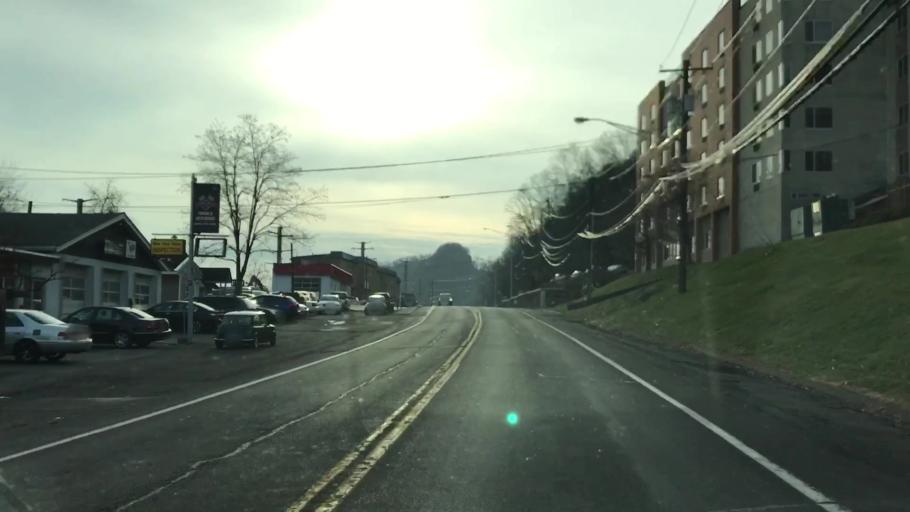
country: US
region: New York
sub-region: Rockland County
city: Haverstraw
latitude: 41.1896
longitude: -73.9625
